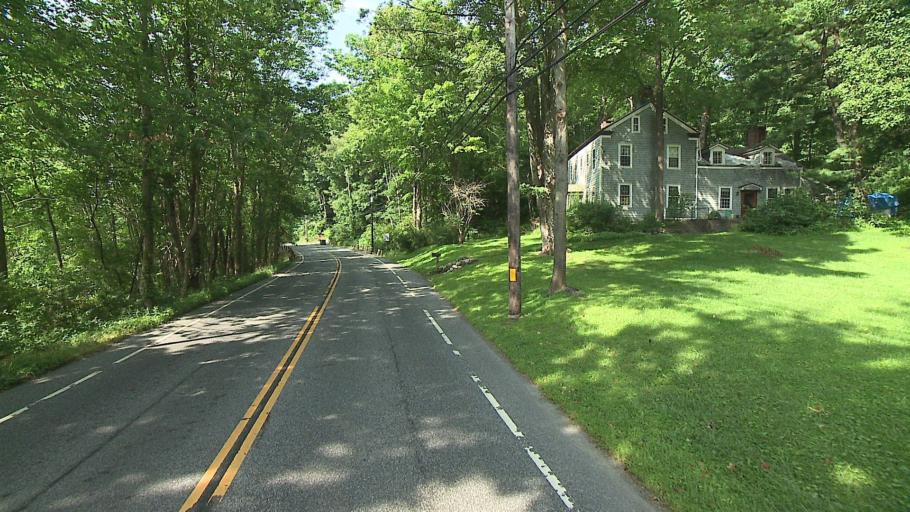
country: US
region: Connecticut
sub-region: Fairfield County
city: Sherman
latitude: 41.5412
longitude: -73.4989
